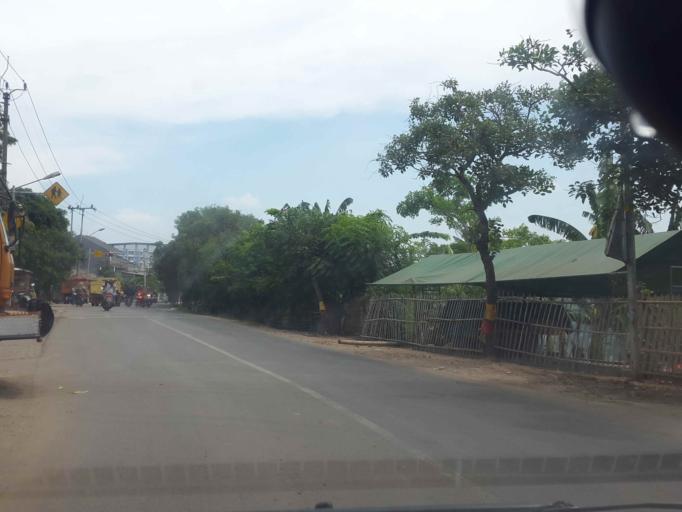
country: ID
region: Banten
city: Tangerang
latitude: -6.1565
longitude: 106.6292
